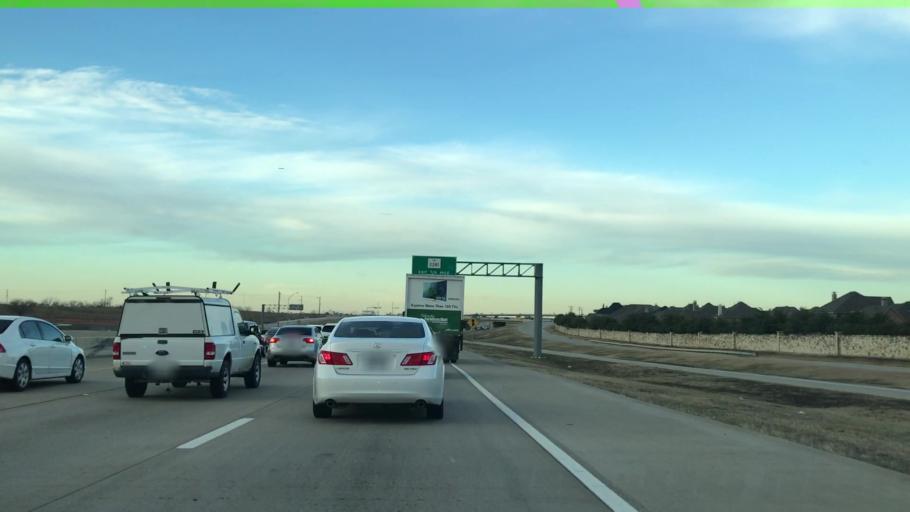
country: US
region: Texas
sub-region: Denton County
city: The Colony
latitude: 33.0411
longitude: -96.9227
